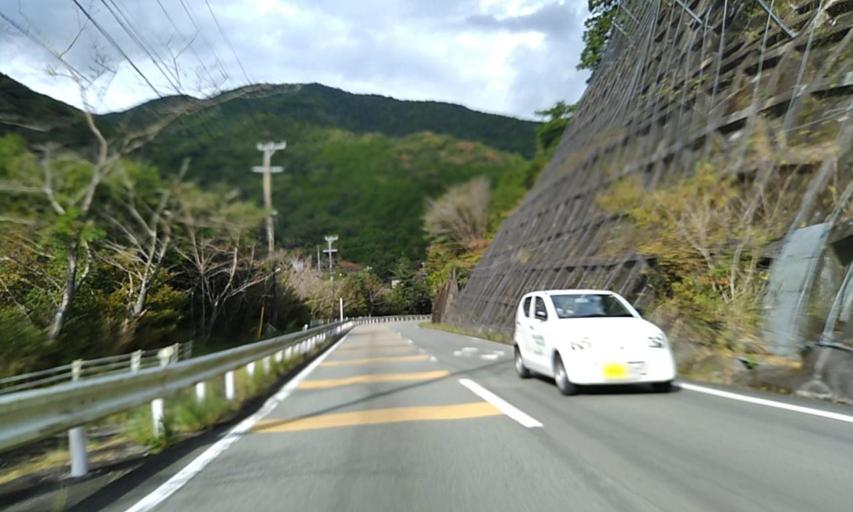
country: JP
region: Mie
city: Ise
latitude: 34.2603
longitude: 136.4819
